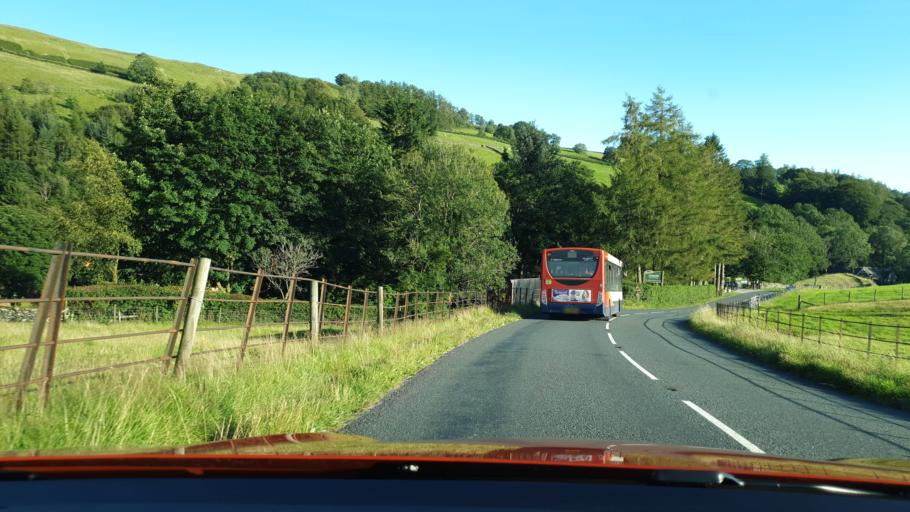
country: GB
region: England
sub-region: Cumbria
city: Windermere
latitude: 54.4201
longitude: -2.9044
